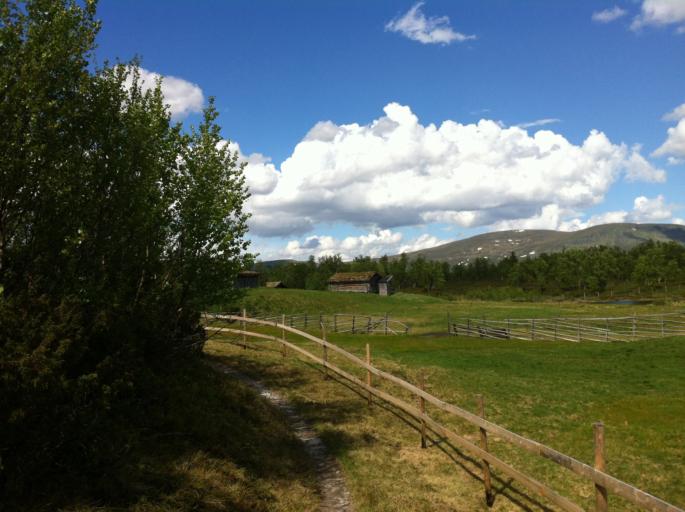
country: NO
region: Sor-Trondelag
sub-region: Tydal
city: Aas
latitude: 62.7143
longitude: 12.4838
